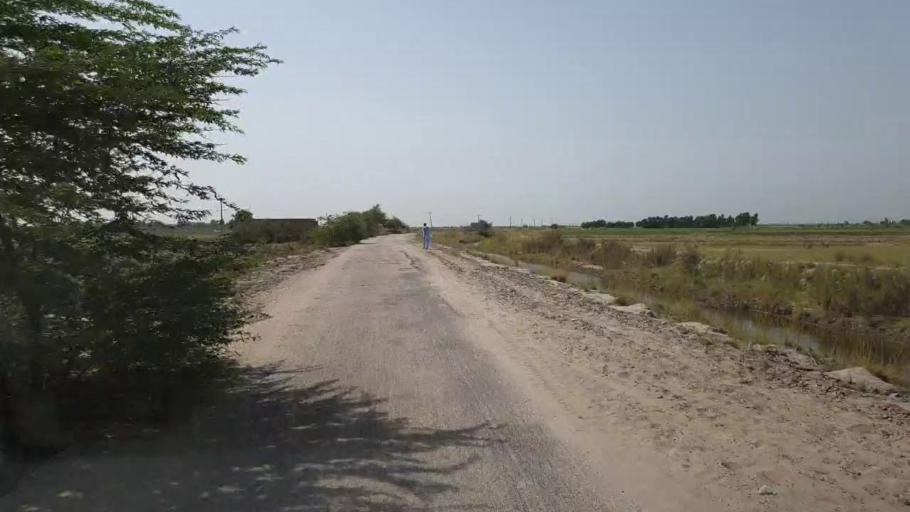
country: PK
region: Sindh
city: Jam Sahib
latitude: 26.4160
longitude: 68.9096
